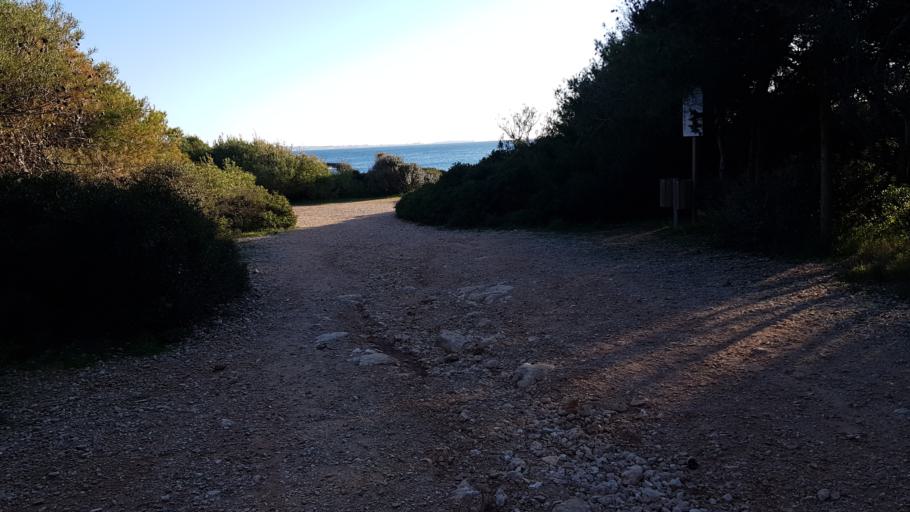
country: IT
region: Apulia
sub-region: Provincia di Lecce
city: Nardo
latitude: 40.1482
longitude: 17.9725
